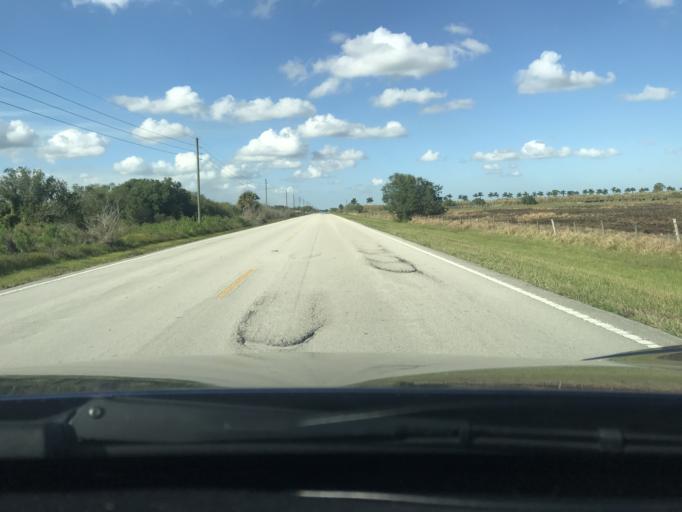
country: US
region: Florida
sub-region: Okeechobee County
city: Taylor Creek
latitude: 27.2561
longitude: -80.6945
